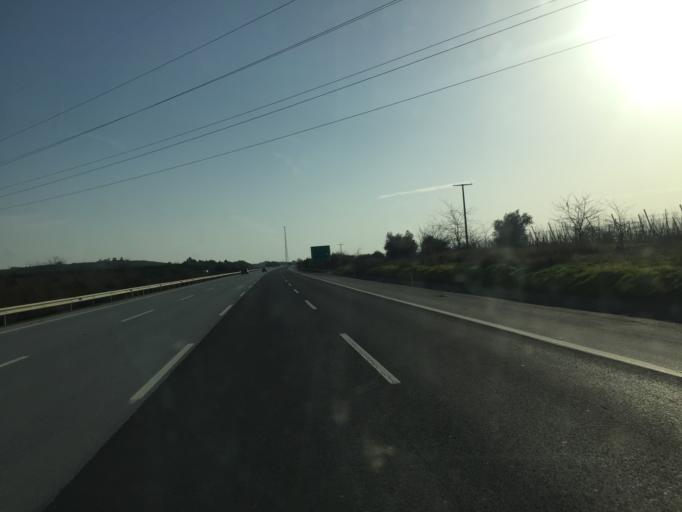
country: TR
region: Mersin
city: Yenice
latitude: 37.0234
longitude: 35.0714
